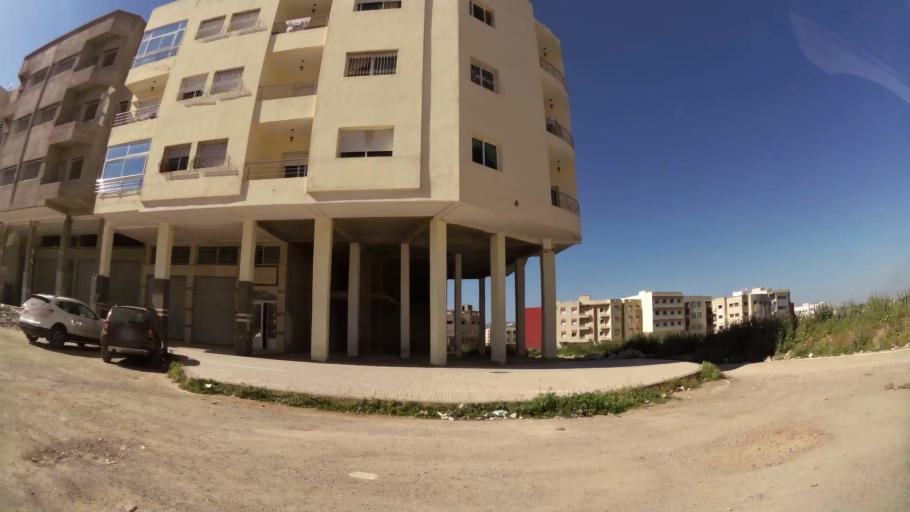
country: MA
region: Fes-Boulemane
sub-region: Fes
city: Fes
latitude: 34.0010
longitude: -5.0055
